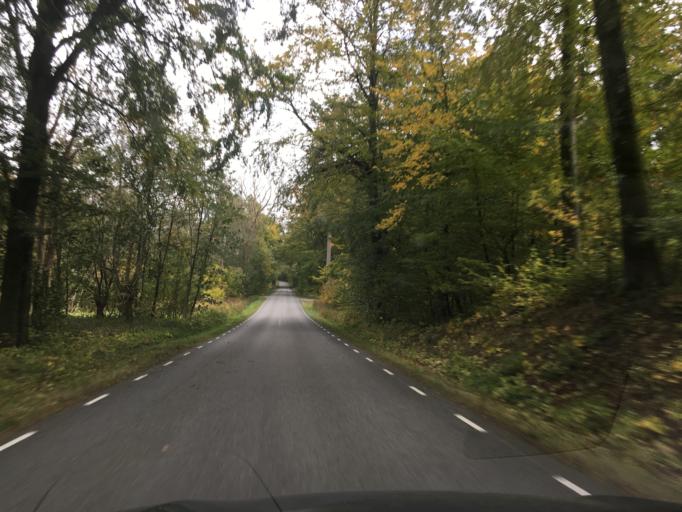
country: SE
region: Skane
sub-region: Tomelilla Kommun
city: Tomelilla
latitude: 55.6425
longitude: 14.0537
